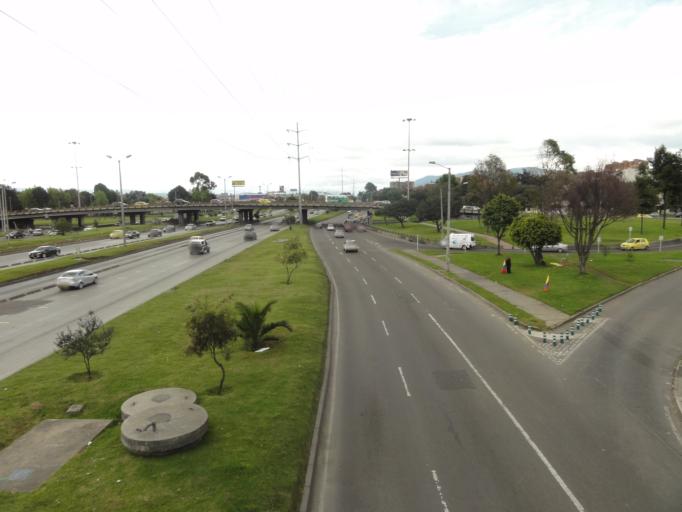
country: CO
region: Bogota D.C.
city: Barrio San Luis
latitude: 4.7055
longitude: -74.0538
